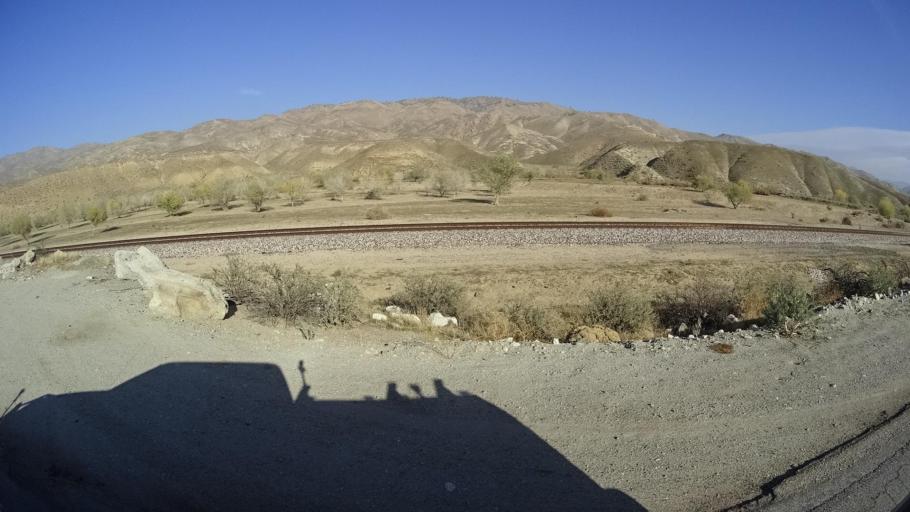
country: US
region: California
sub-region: Kern County
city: Arvin
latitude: 35.3182
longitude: -118.7053
